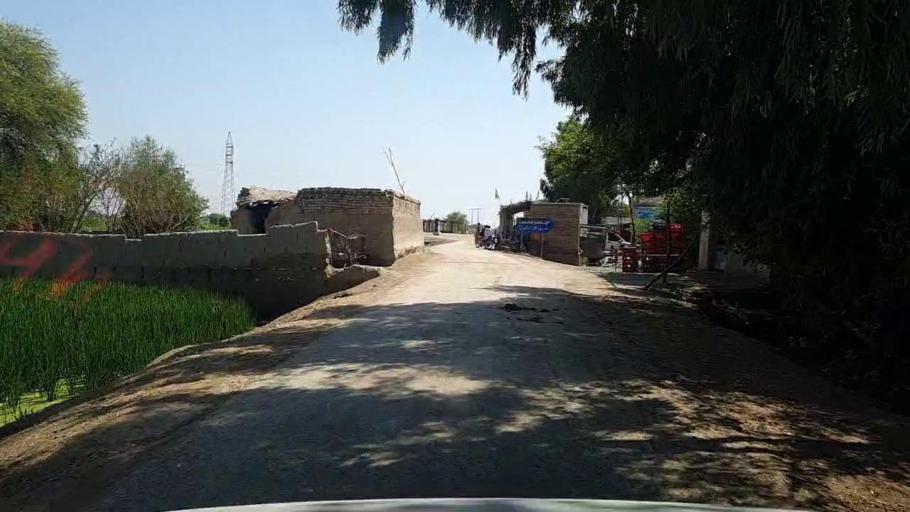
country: PK
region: Sindh
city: Kandhkot
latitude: 28.3194
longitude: 69.3399
